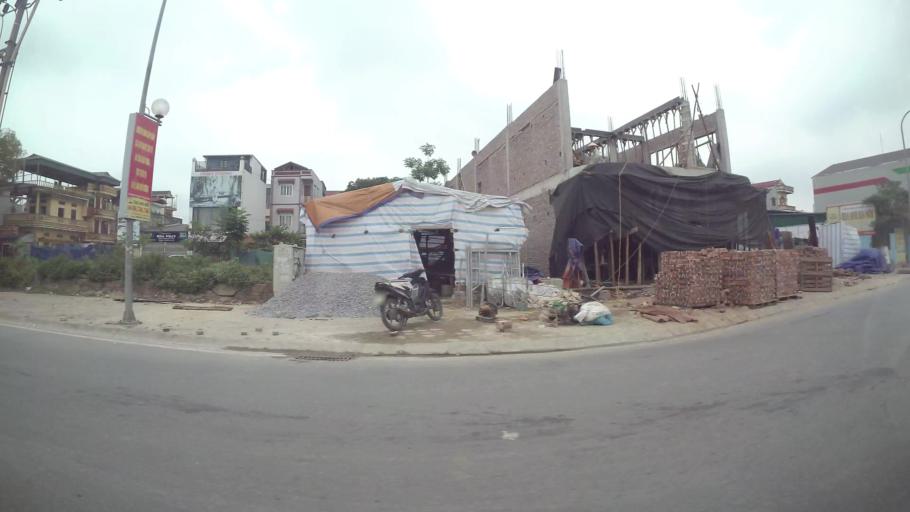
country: VN
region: Ha Noi
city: Trau Quy
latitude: 21.0394
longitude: 105.9289
